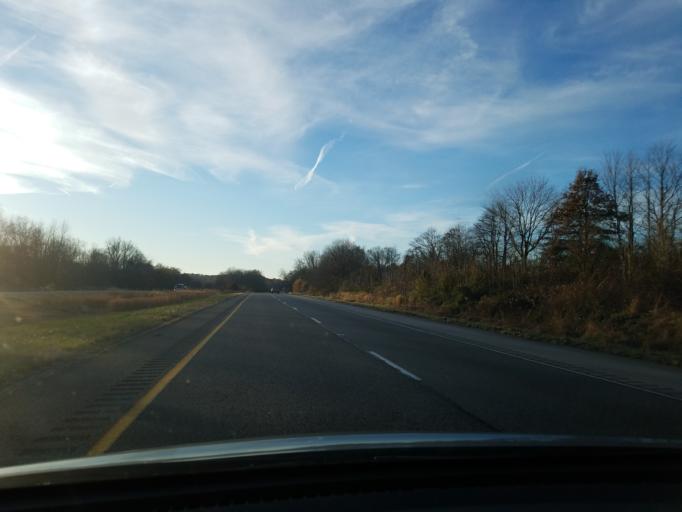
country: US
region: Indiana
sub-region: Spencer County
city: Dale
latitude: 38.1986
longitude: -87.1647
